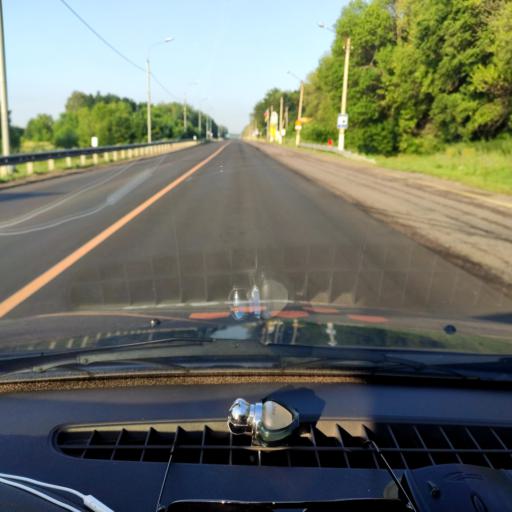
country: RU
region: Lipetsk
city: Izmalkovo
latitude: 52.4721
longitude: 38.0256
